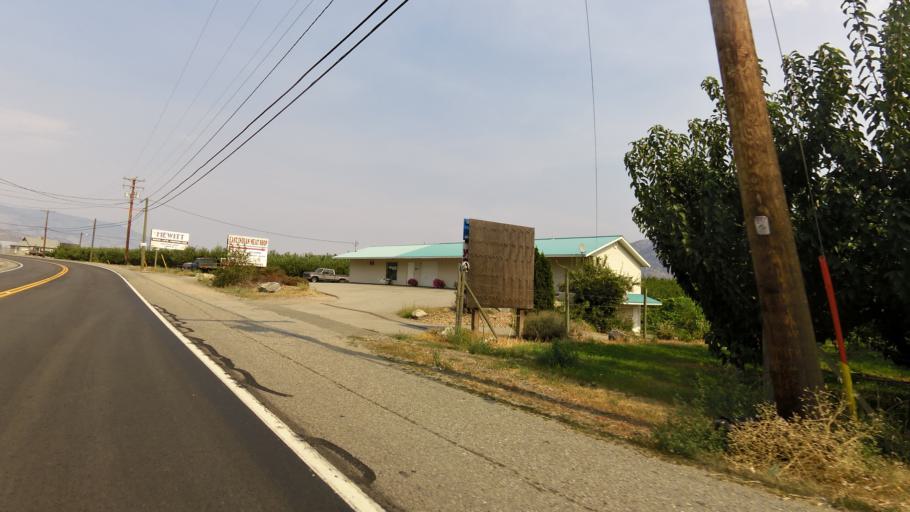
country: CA
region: British Columbia
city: Osoyoos
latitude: 49.0412
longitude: -119.4836
